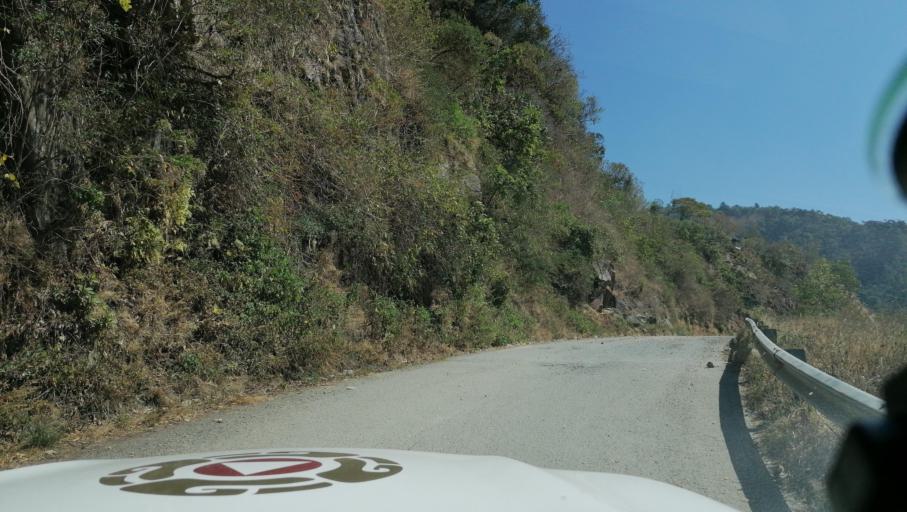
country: GT
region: San Marcos
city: Tacana
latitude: 15.1919
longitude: -92.1857
